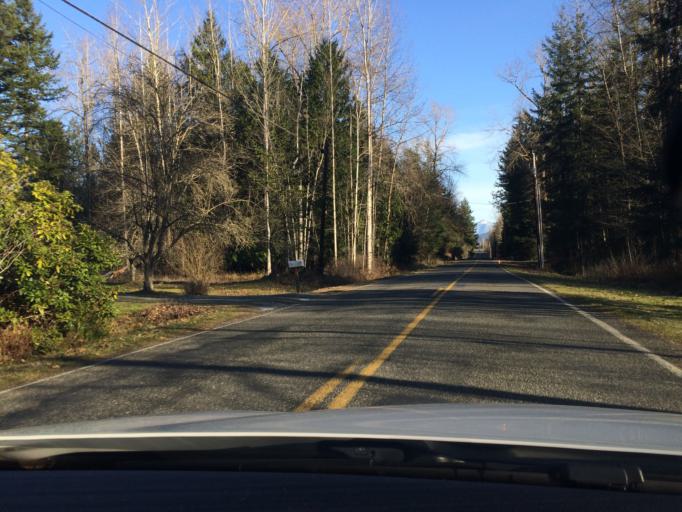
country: US
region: Washington
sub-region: Whatcom County
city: Geneva
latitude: 48.8186
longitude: -122.4269
